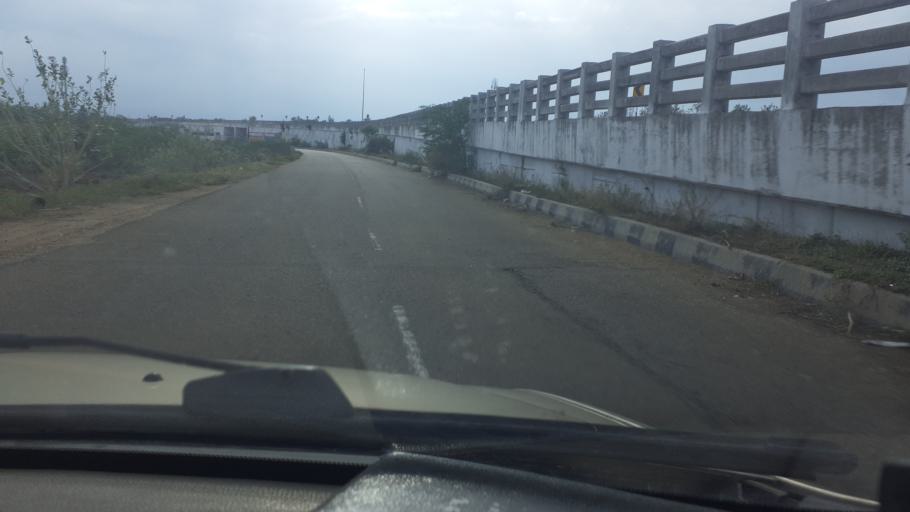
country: IN
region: Tamil Nadu
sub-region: Tirunelveli Kattabo
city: Tirunelveli
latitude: 8.6603
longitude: 77.7171
